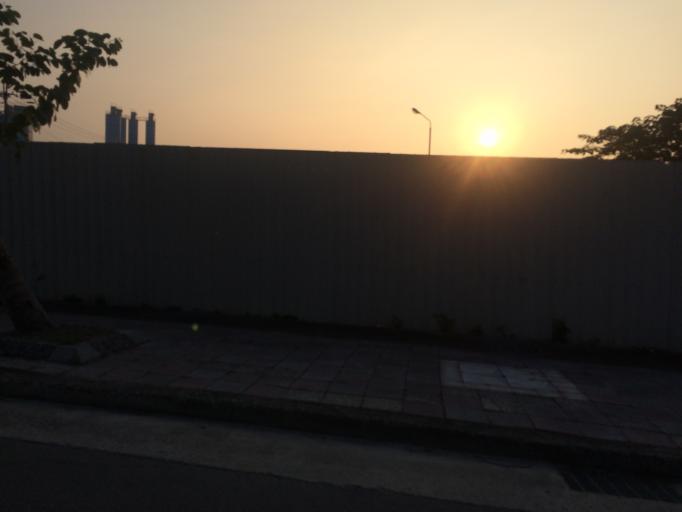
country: TW
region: Taiwan
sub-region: Hsinchu
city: Hsinchu
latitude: 24.7323
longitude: 120.9148
